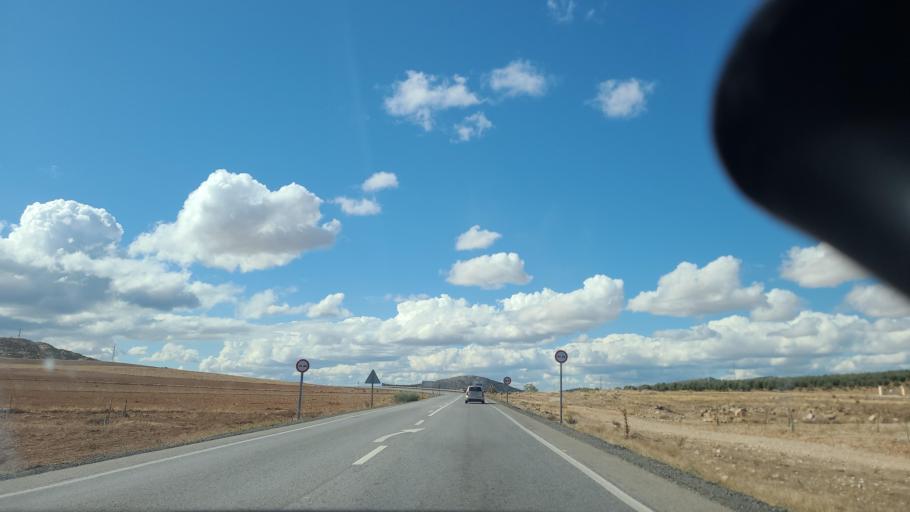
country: ES
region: Andalusia
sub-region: Provincia de Granada
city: Gobernador
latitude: 37.4121
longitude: -3.3580
